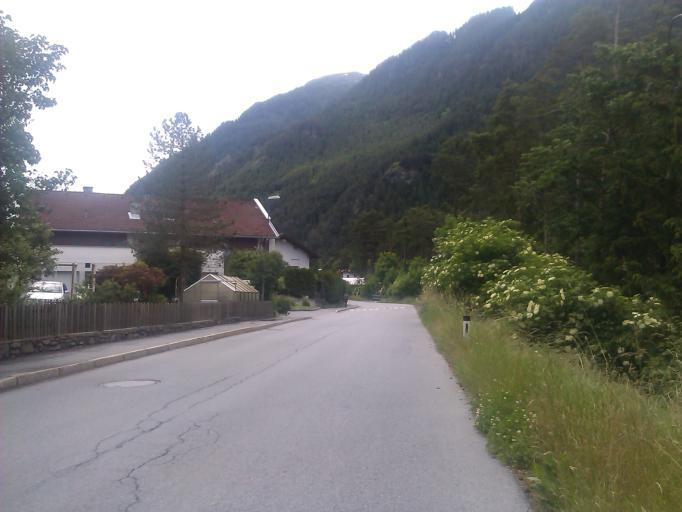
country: AT
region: Tyrol
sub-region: Politischer Bezirk Landeck
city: Serfaus
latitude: 47.0220
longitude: 10.6140
